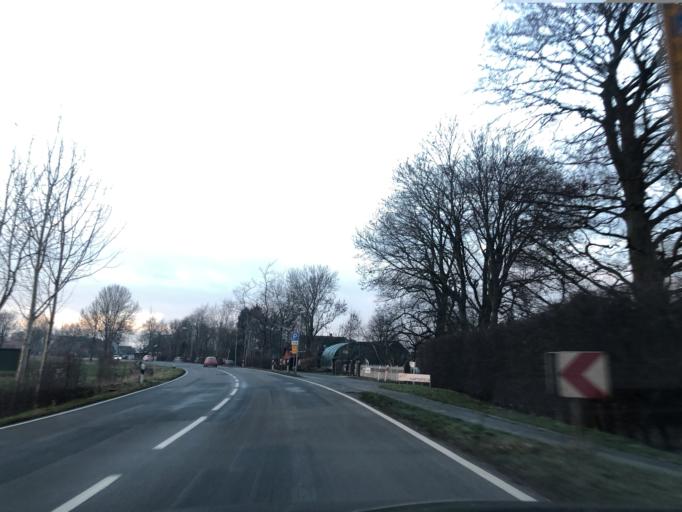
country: DE
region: Lower Saxony
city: Lemwerder
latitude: 53.1397
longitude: 8.5954
